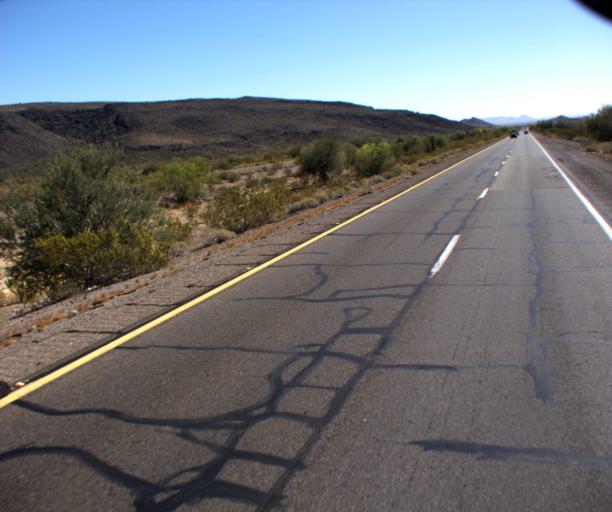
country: US
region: Arizona
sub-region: La Paz County
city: Quartzsite
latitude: 33.6501
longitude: -113.9163
